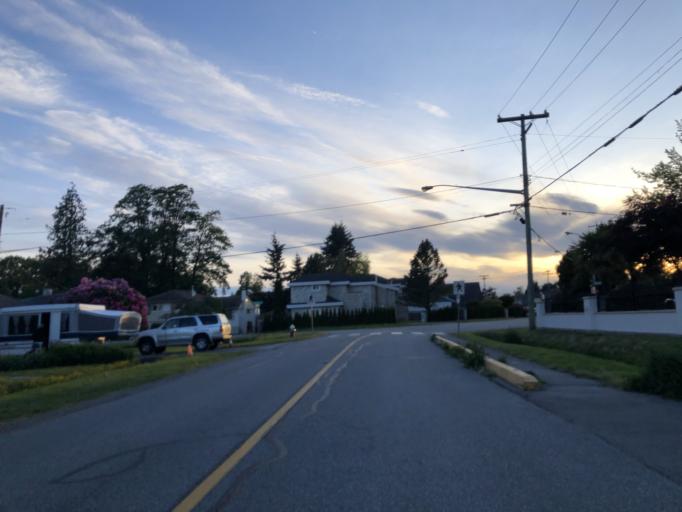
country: CA
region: British Columbia
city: Richmond
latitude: 49.1432
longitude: -123.1231
